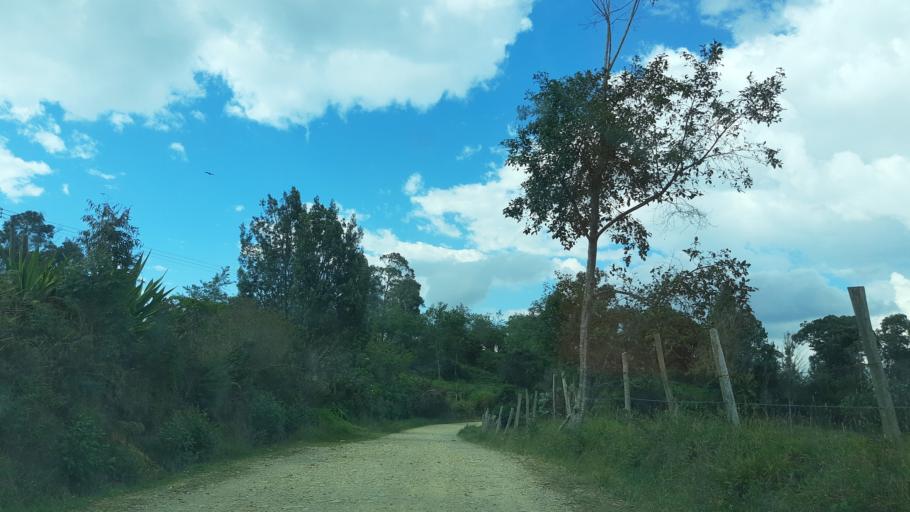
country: CO
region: Boyaca
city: Santa Sofia
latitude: 5.7416
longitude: -73.5525
